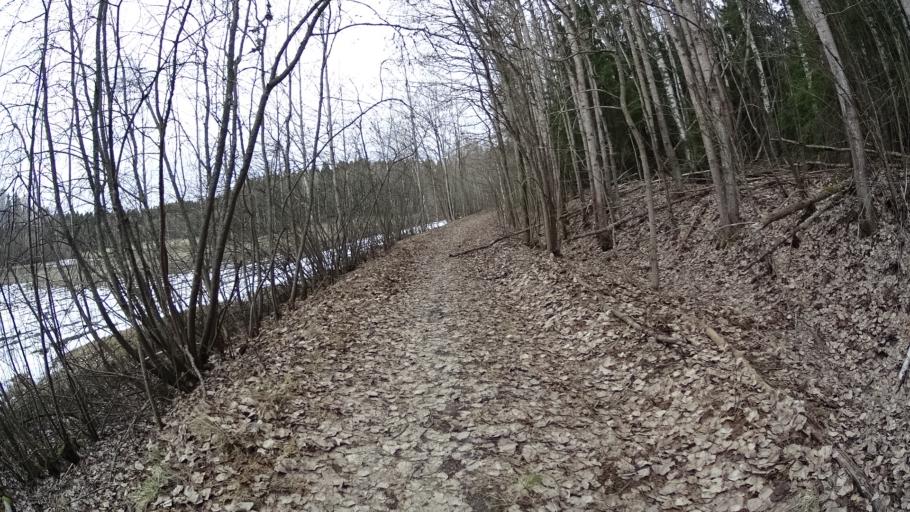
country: FI
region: Uusimaa
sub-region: Helsinki
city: Kilo
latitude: 60.2814
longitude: 24.8032
